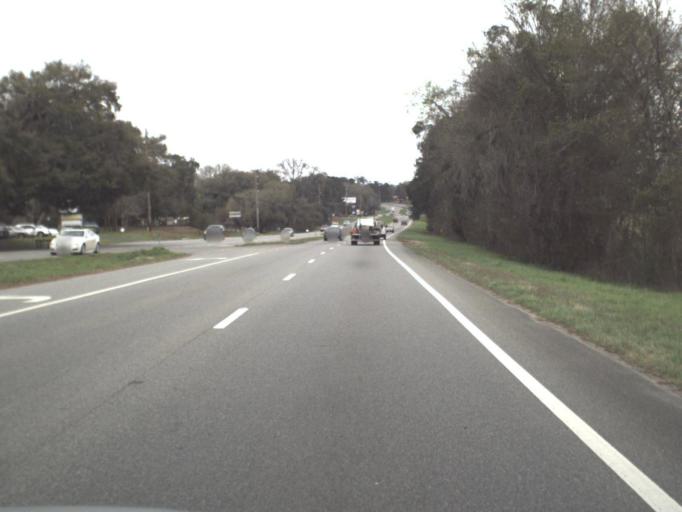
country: US
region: Florida
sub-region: Leon County
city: Tallahassee
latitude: 30.5191
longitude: -84.3491
